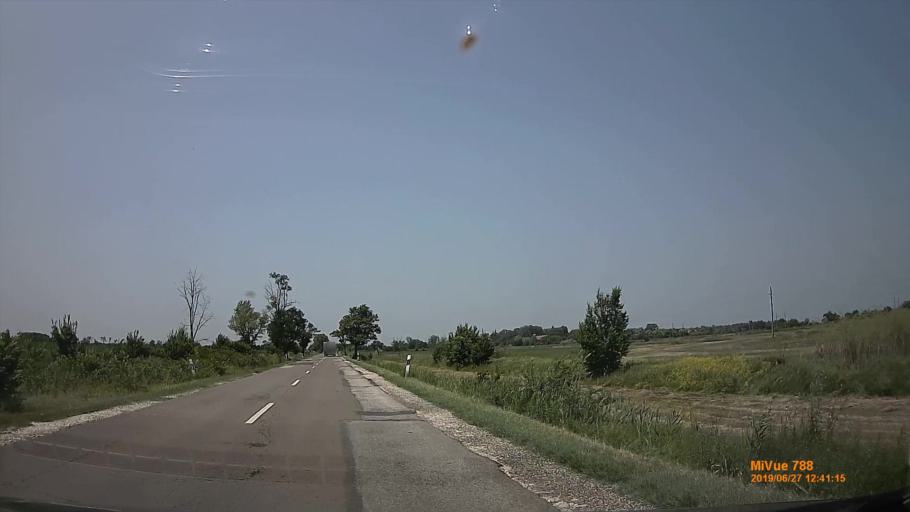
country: HU
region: Pest
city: Tortel
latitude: 47.1799
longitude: 19.8996
